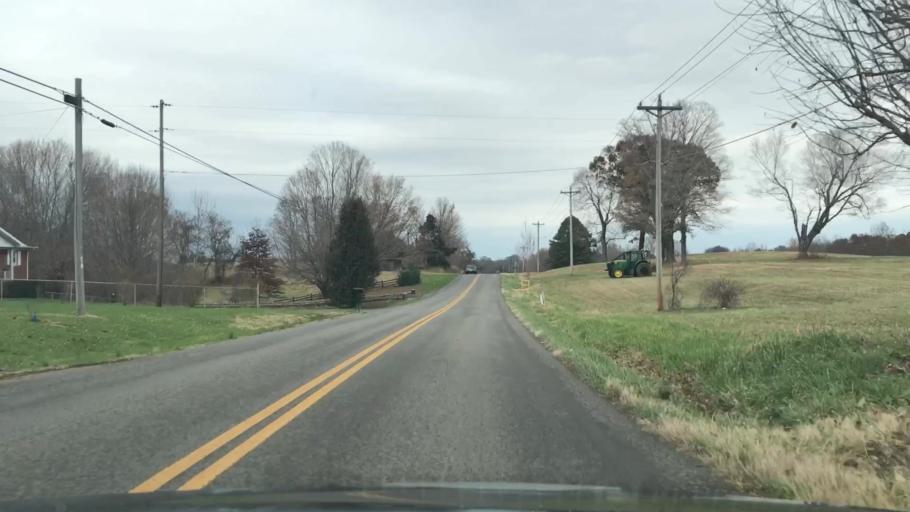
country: US
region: Kentucky
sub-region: Metcalfe County
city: Edmonton
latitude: 36.9516
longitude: -85.6148
